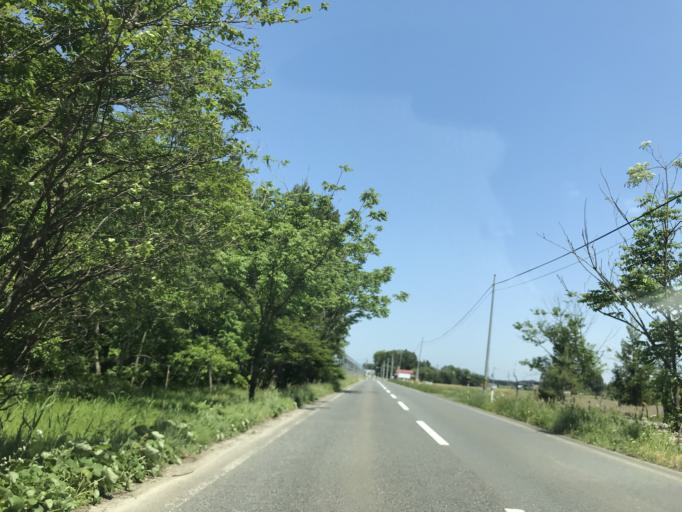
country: JP
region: Iwate
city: Kitakami
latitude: 39.2506
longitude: 141.0655
